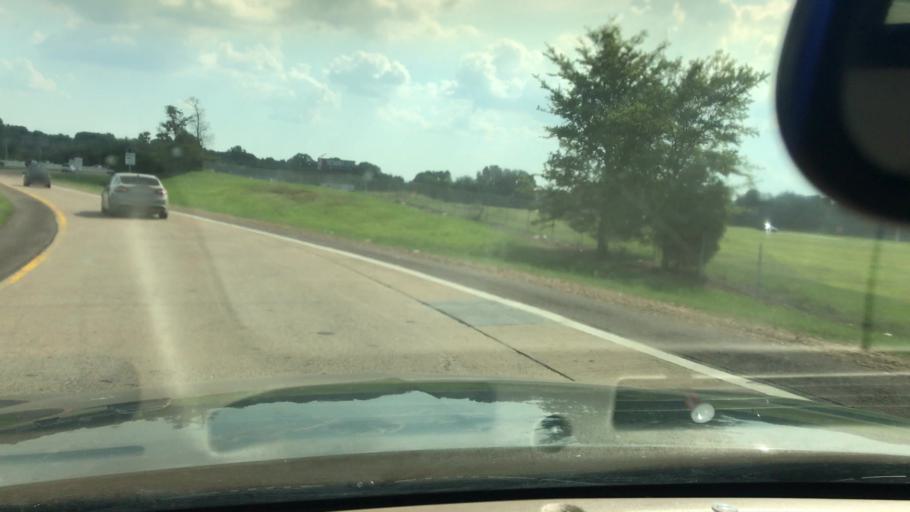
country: US
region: Tennessee
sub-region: Shelby County
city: Bartlett
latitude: 35.1862
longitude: -89.8149
